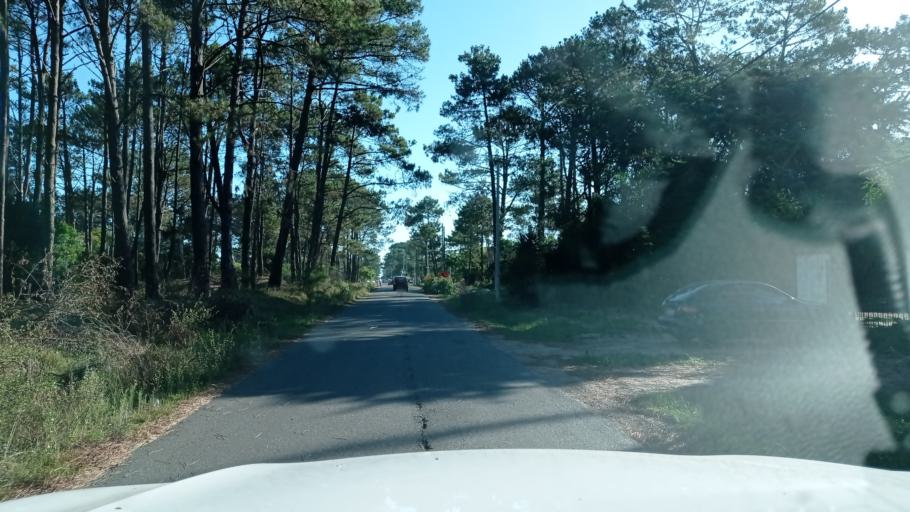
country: UY
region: Canelones
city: Pando
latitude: -34.8012
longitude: -55.9079
